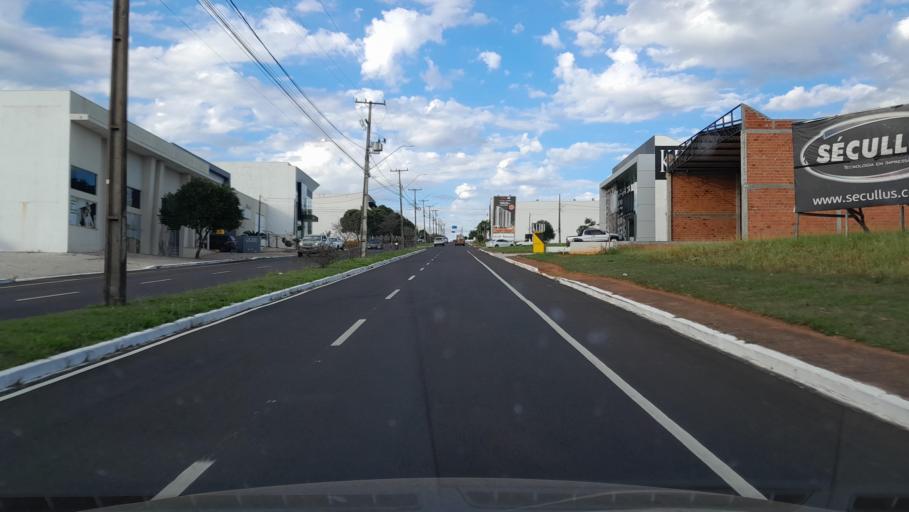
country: BR
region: Parana
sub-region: Umuarama
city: Umuarama
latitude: -23.7535
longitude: -53.2777
